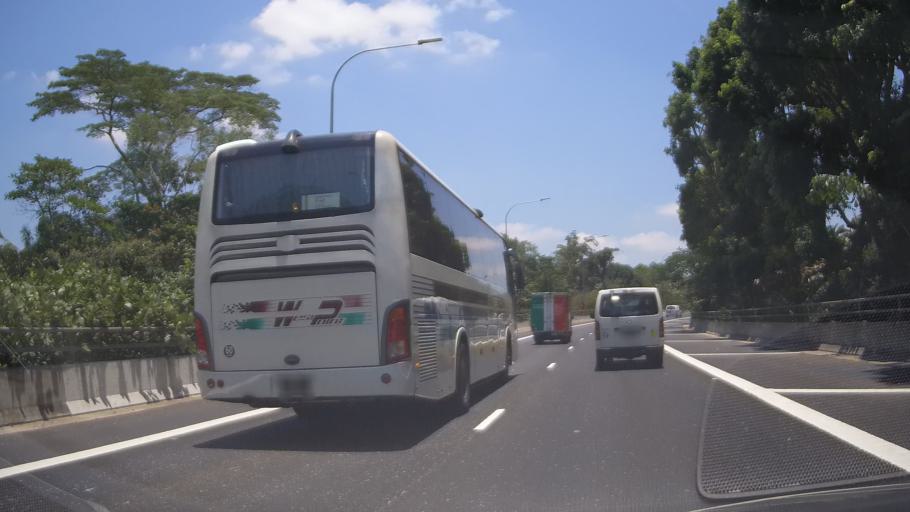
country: MY
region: Johor
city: Johor Bahru
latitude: 1.3935
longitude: 103.7749
